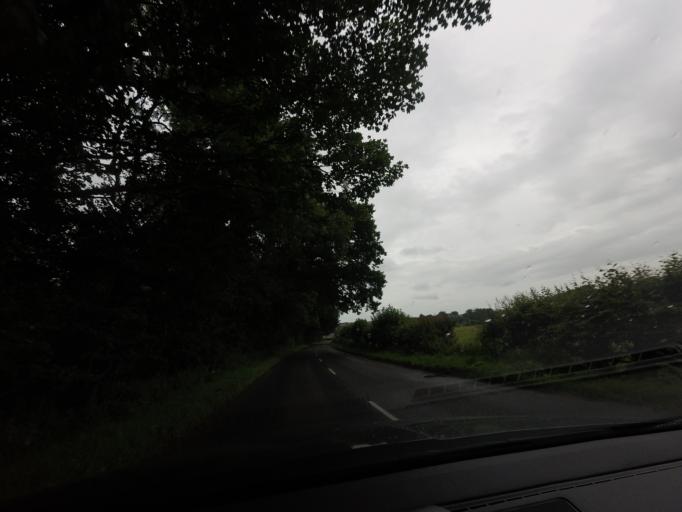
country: GB
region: Scotland
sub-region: Aberdeenshire
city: Turriff
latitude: 57.5408
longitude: -2.4853
